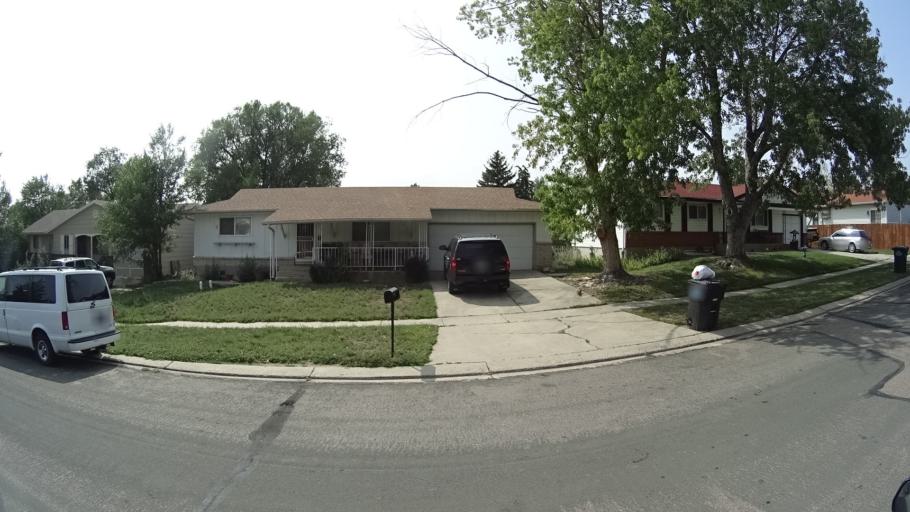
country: US
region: Colorado
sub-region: El Paso County
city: Stratmoor
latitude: 38.8046
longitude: -104.7709
